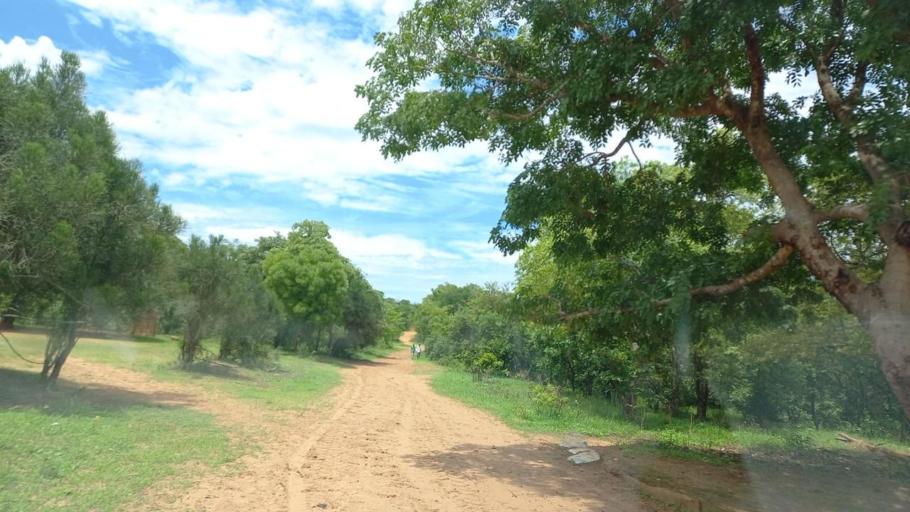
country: ZM
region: North-Western
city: Kabompo
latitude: -13.6107
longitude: 24.2439
